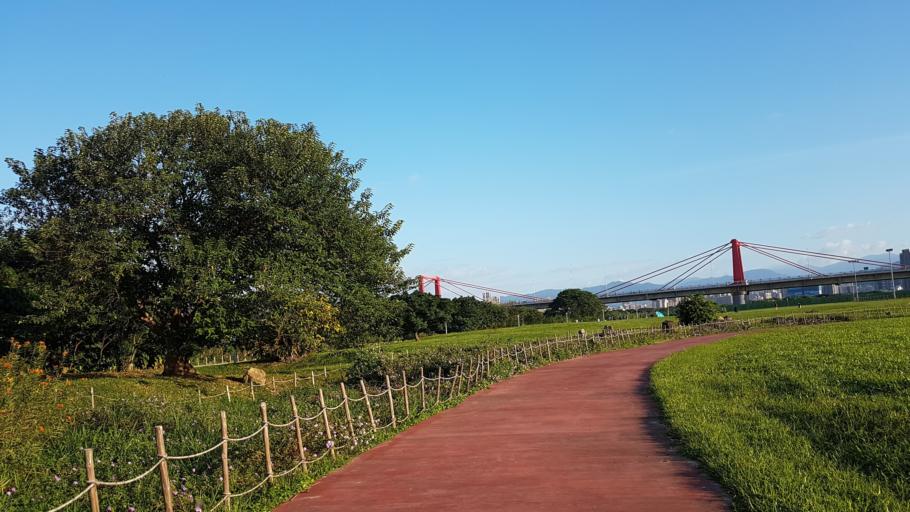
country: TW
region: Taipei
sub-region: Taipei
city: Banqiao
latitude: 25.0255
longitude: 121.4861
